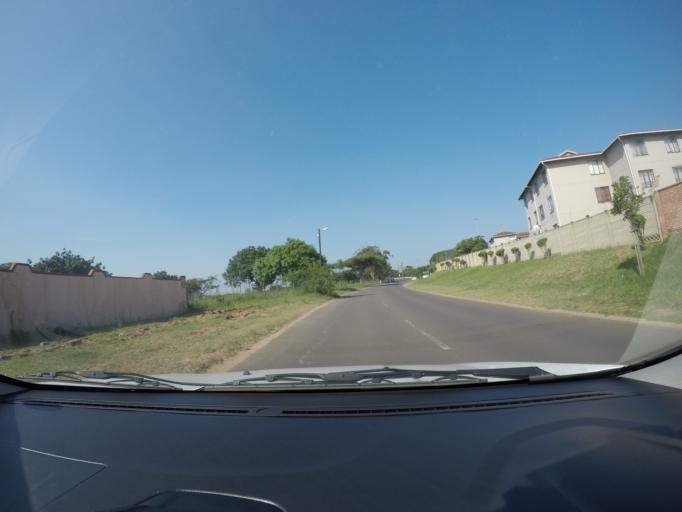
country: ZA
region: KwaZulu-Natal
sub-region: uThungulu District Municipality
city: Richards Bay
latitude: -28.7231
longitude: 32.0388
